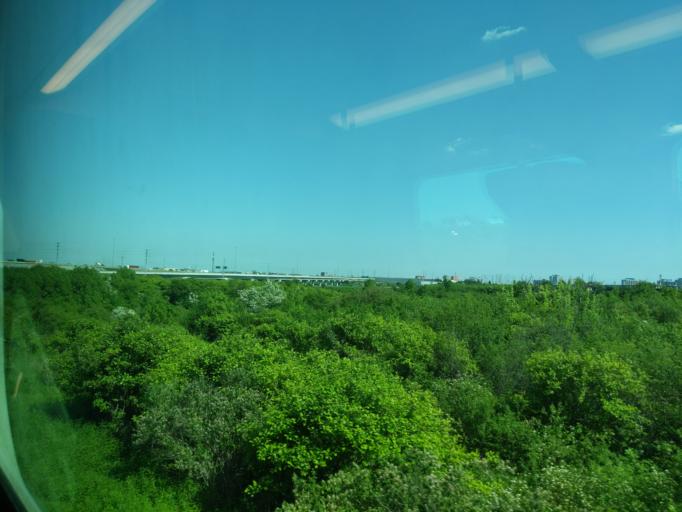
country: CA
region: Ontario
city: Etobicoke
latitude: 43.7052
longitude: -79.6187
